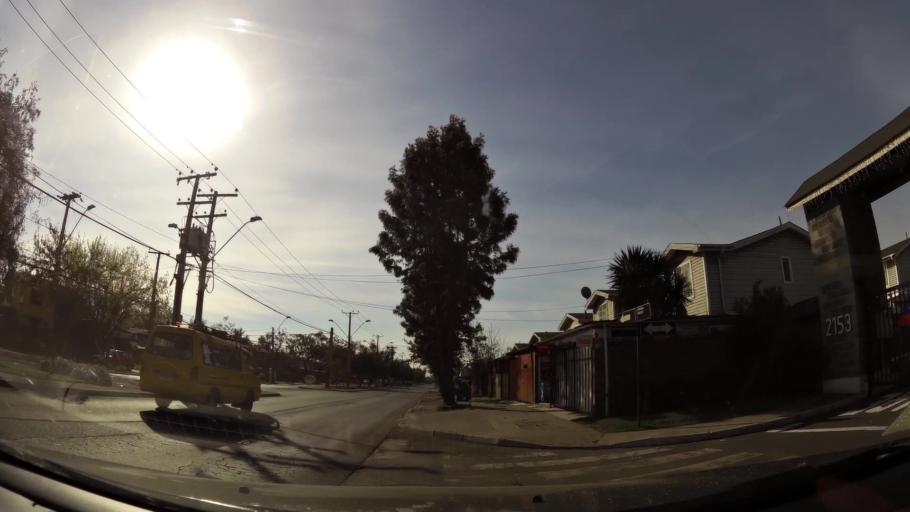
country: CL
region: Santiago Metropolitan
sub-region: Provincia de Cordillera
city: Puente Alto
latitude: -33.5910
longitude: -70.5611
